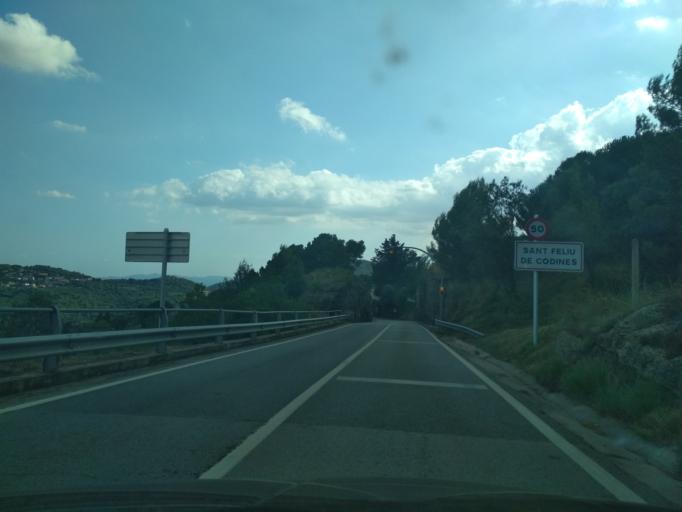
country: ES
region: Catalonia
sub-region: Provincia de Barcelona
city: Sant Feliu de Codines
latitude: 41.6933
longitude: 2.1710
